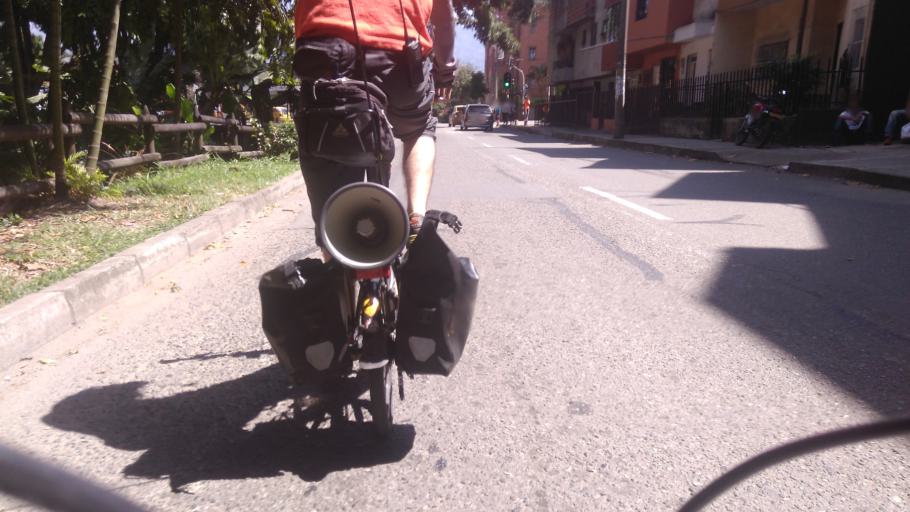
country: CO
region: Antioquia
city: Medellin
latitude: 6.2290
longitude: -75.5968
